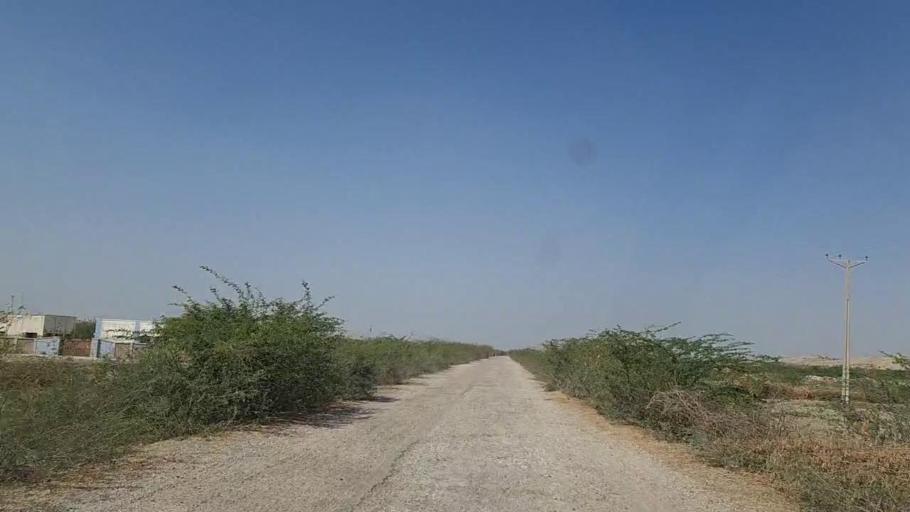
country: PK
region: Sindh
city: Naukot
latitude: 24.6265
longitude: 69.2888
